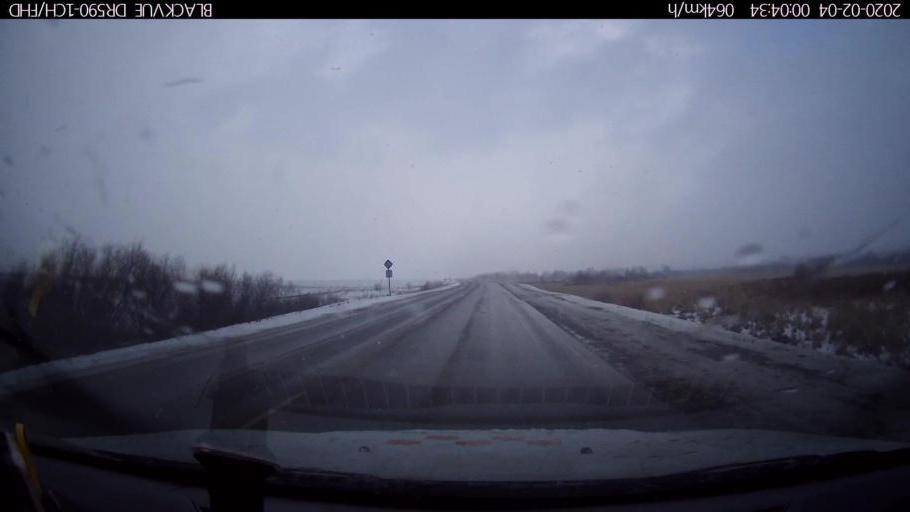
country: RU
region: Nizjnij Novgorod
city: Dal'neye Konstantinovo
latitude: 55.8278
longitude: 44.1196
